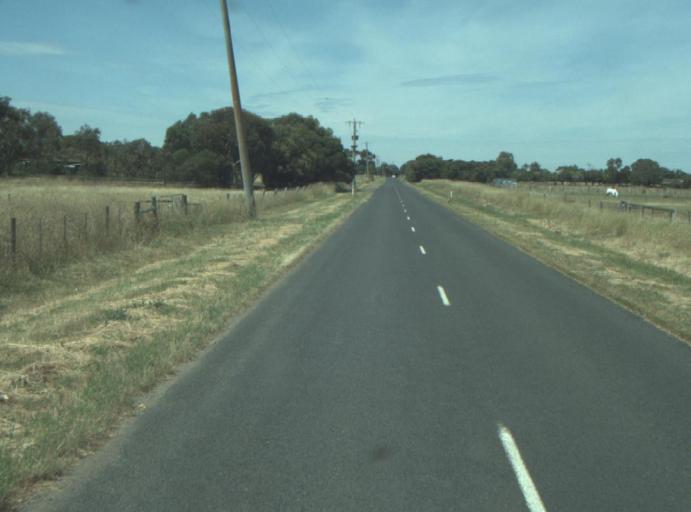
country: AU
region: Victoria
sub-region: Greater Geelong
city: Leopold
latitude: -38.1664
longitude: 144.4550
